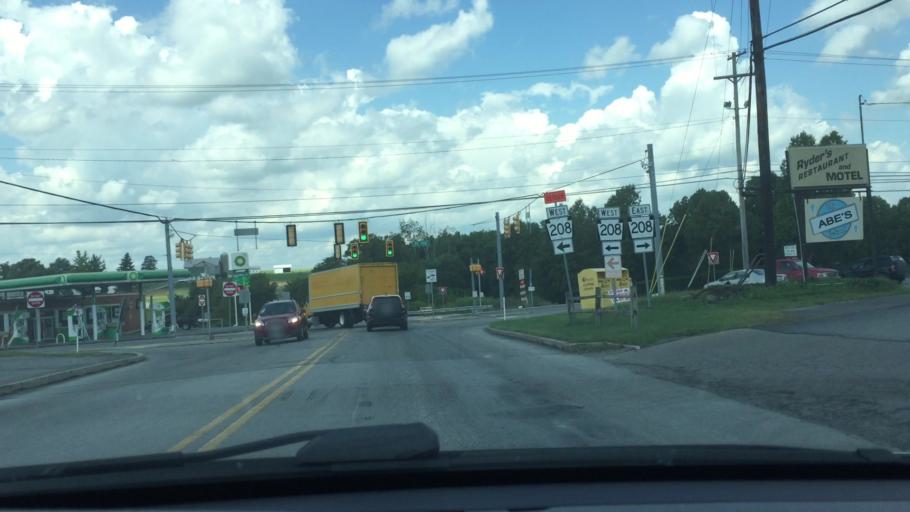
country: US
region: Pennsylvania
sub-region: Lawrence County
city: New Wilmington
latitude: 41.1201
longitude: -80.3596
